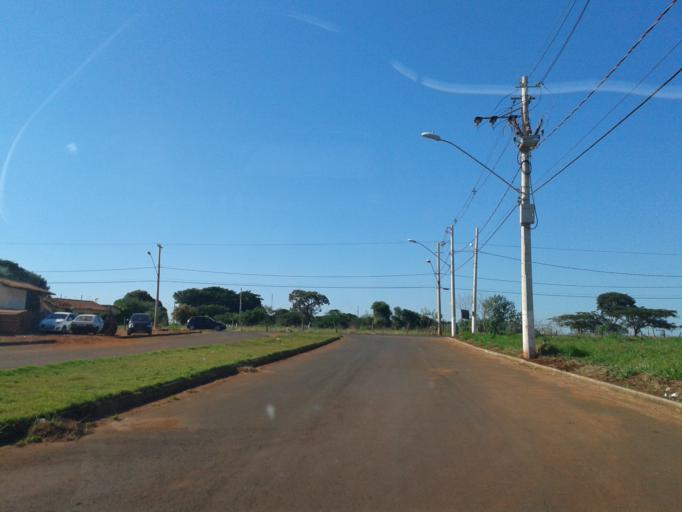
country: BR
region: Minas Gerais
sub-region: Ituiutaba
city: Ituiutaba
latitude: -18.9912
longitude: -49.4870
